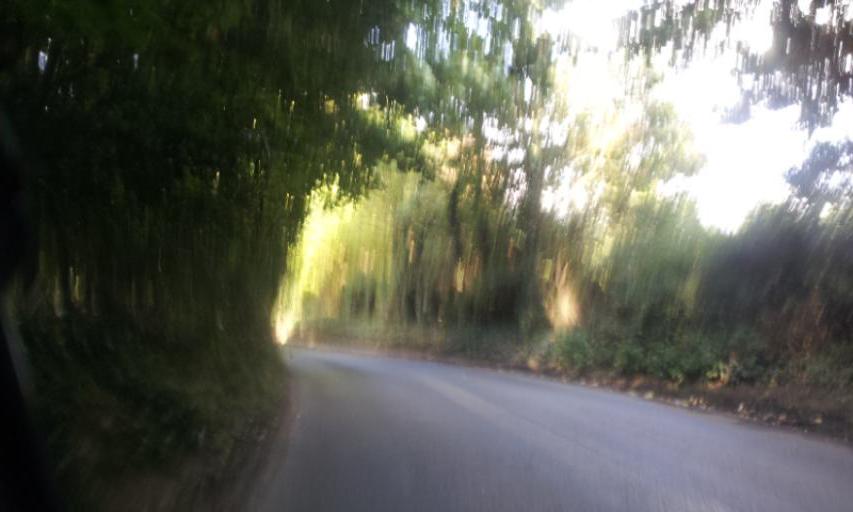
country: GB
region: England
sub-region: Kent
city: Yalding
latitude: 51.2231
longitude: 0.4700
